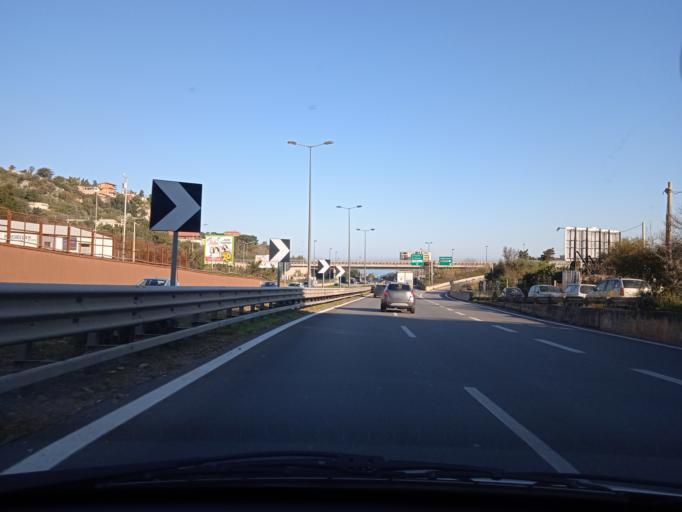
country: IT
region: Sicily
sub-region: Palermo
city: Isola delle Femmine
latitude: 38.1886
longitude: 13.2835
